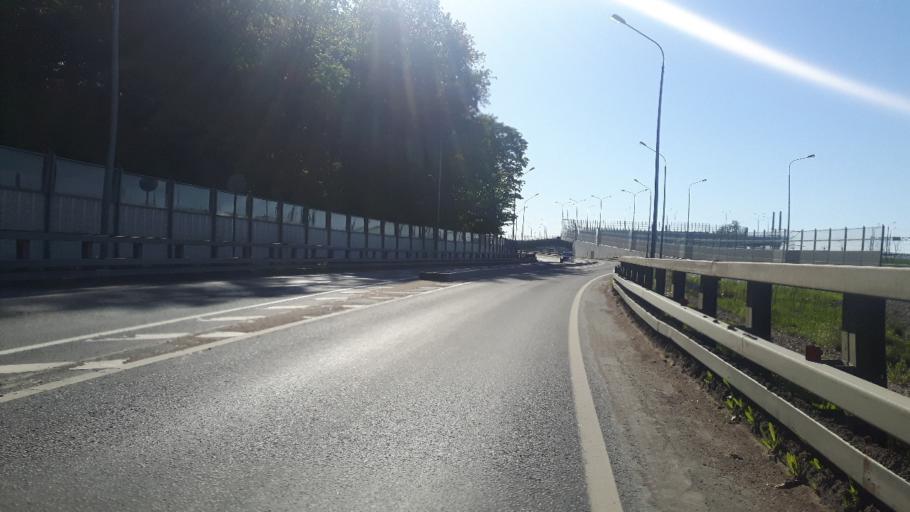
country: RU
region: St.-Petersburg
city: Lomonosov
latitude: 59.9262
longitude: 29.6787
